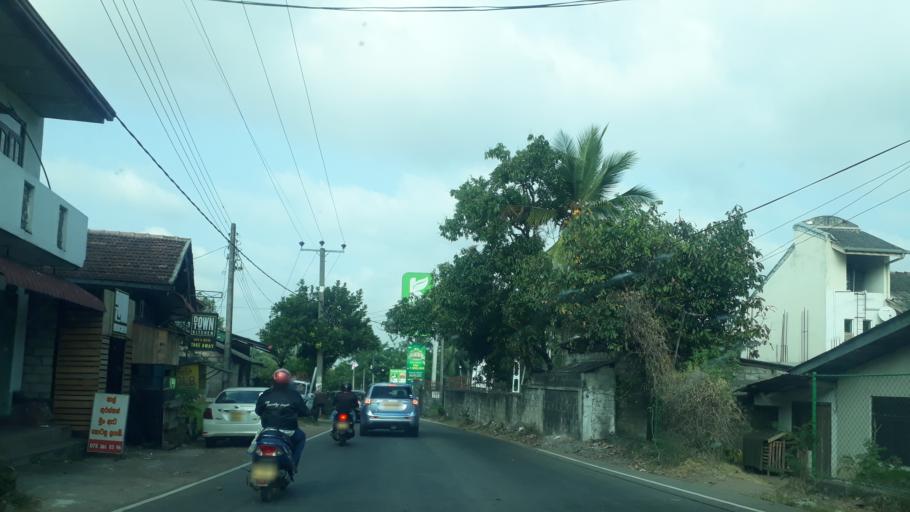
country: LK
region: Western
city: Battaramulla South
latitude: 6.8958
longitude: 79.9413
